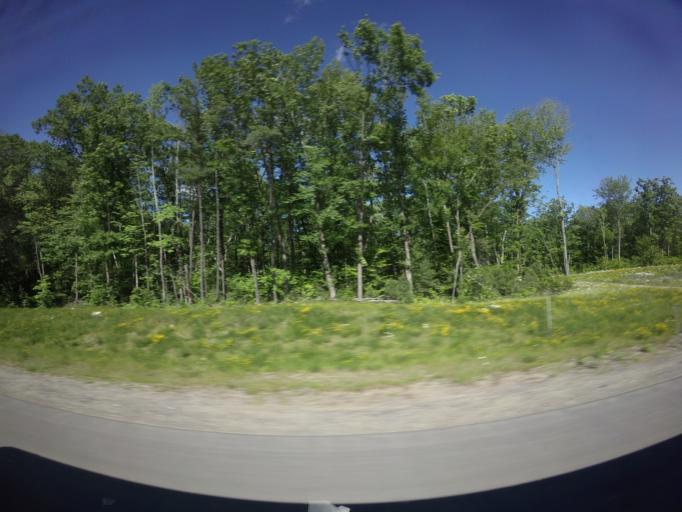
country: US
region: New Hampshire
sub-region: Rockingham County
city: Londonderry
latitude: 42.9294
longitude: -71.3793
